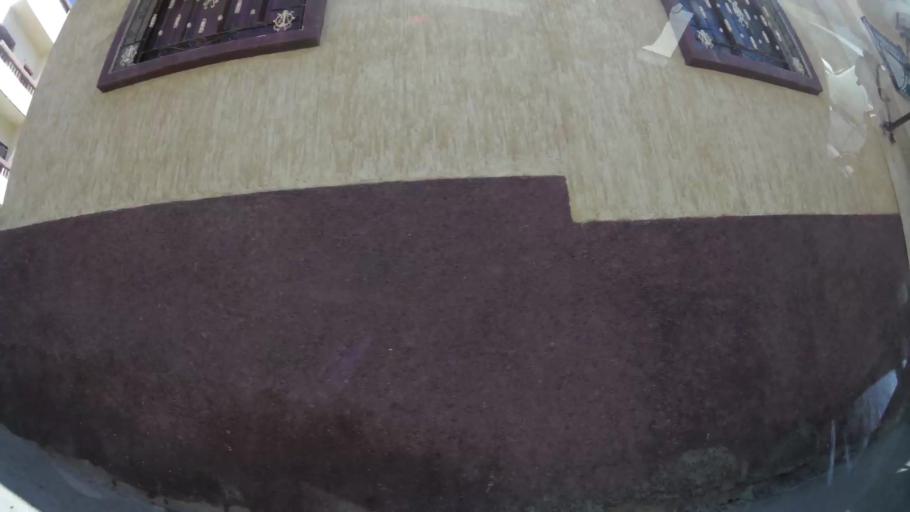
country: MA
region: Oued ed Dahab-Lagouira
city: Dakhla
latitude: 30.4409
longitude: -9.5542
